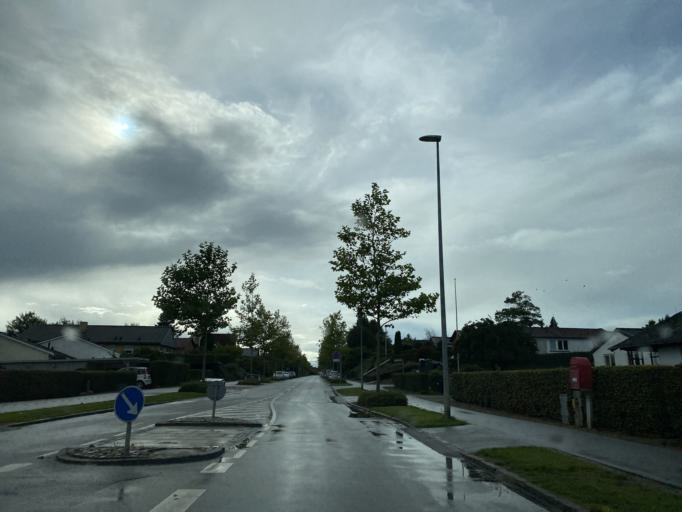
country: DK
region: South Denmark
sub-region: Haderslev Kommune
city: Haderslev
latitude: 55.2552
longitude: 9.4645
